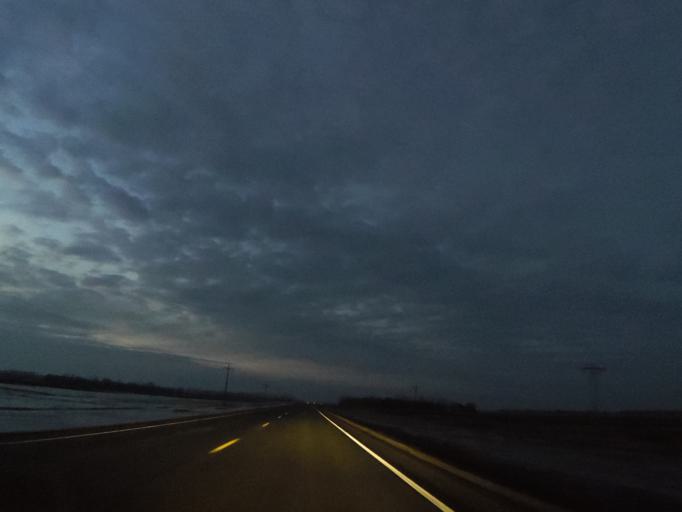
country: US
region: North Dakota
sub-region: Walsh County
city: Park River
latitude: 48.2851
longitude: -97.6226
